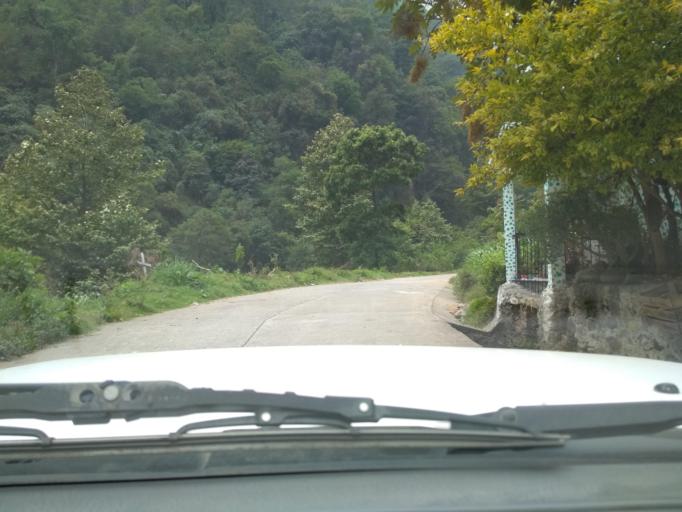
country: MX
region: Veracruz
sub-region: La Perla
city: Metlac Hernandez (Metlac Primero)
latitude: 18.9897
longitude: -97.1263
